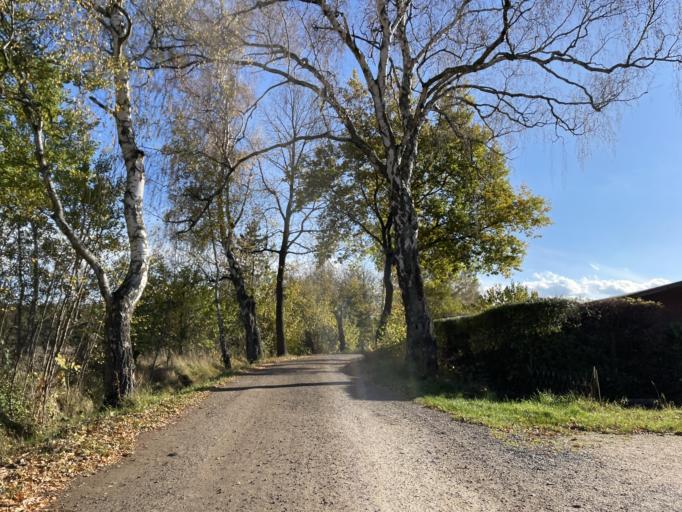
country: DE
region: Lower Saxony
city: Lueneburg
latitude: 53.2235
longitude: 10.4171
